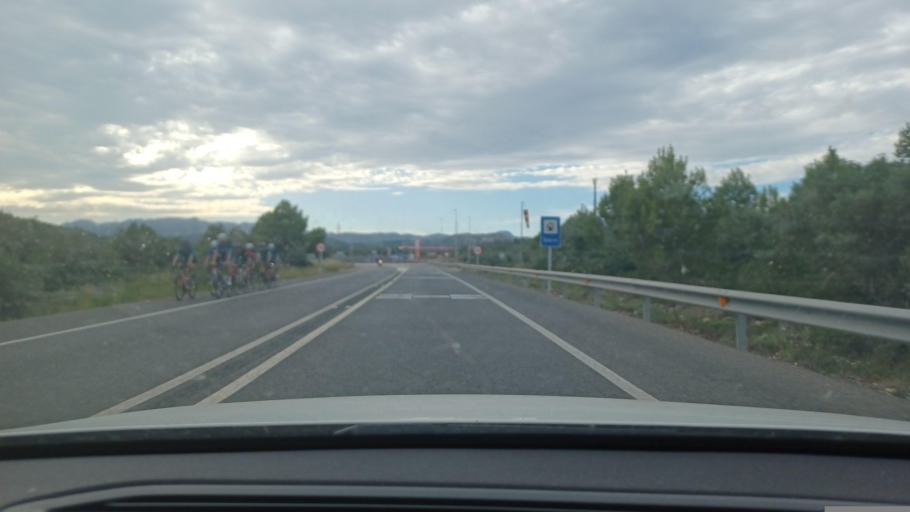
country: ES
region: Catalonia
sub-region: Provincia de Tarragona
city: El Perello
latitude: 40.8960
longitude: 0.7529
